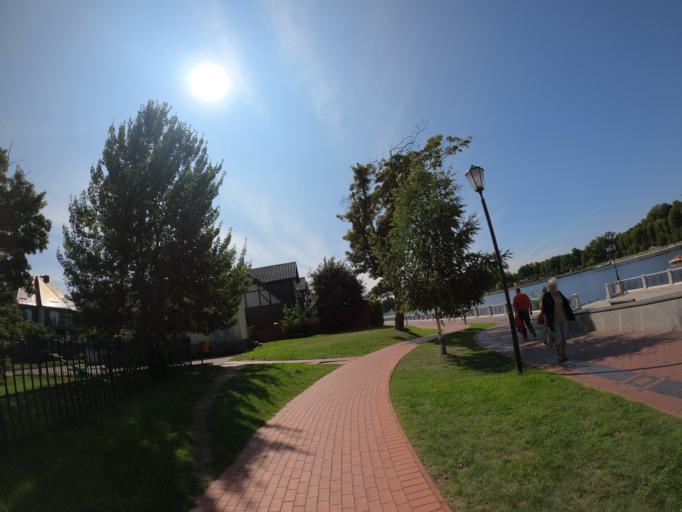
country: RU
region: Kaliningrad
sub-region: Gorod Kaliningrad
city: Kaliningrad
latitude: 54.7274
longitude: 20.5202
